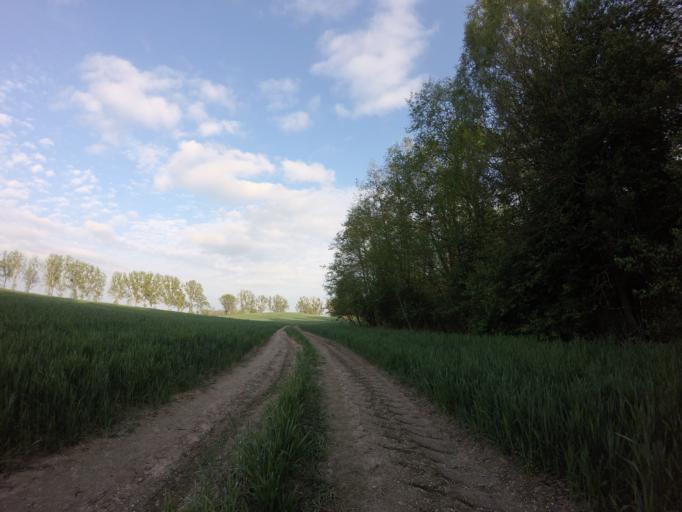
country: PL
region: West Pomeranian Voivodeship
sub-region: Powiat choszczenski
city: Choszczno
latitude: 53.1530
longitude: 15.3461
